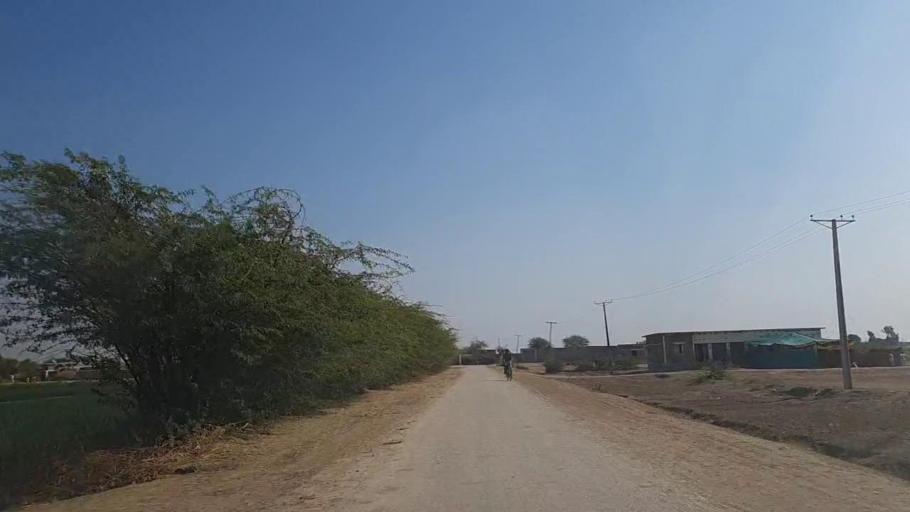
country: PK
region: Sindh
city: Digri
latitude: 25.1584
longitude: 69.1376
